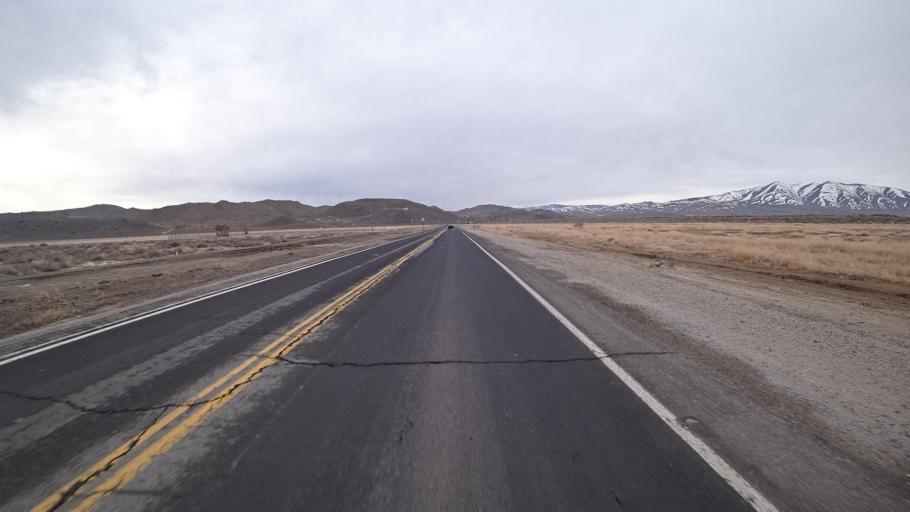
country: US
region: Nevada
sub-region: Washoe County
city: Lemmon Valley
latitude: 39.6584
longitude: -119.8267
